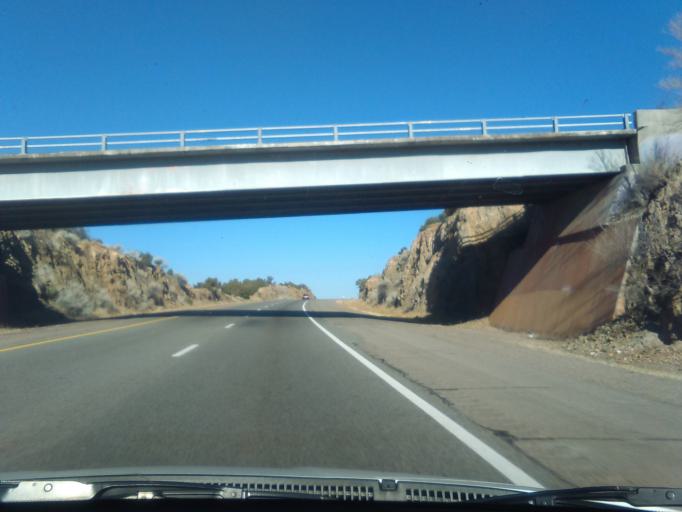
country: US
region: New Mexico
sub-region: Santa Fe County
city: Eldorado at Santa Fe
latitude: 35.5801
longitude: -105.8984
